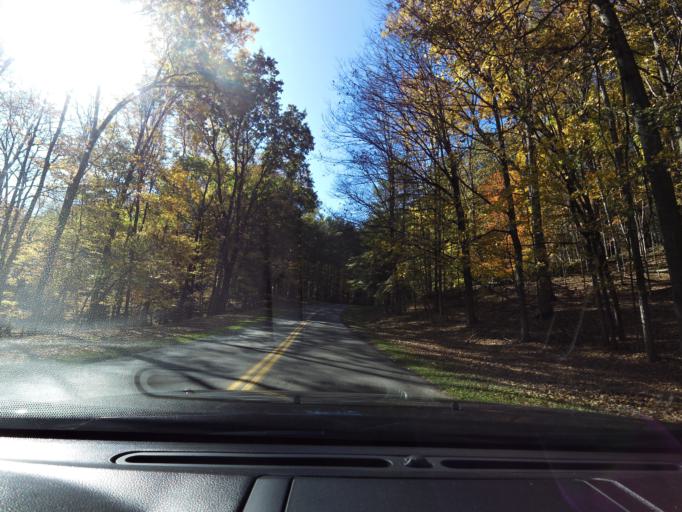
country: US
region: New York
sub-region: Wyoming County
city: Castile
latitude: 42.5938
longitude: -78.0241
